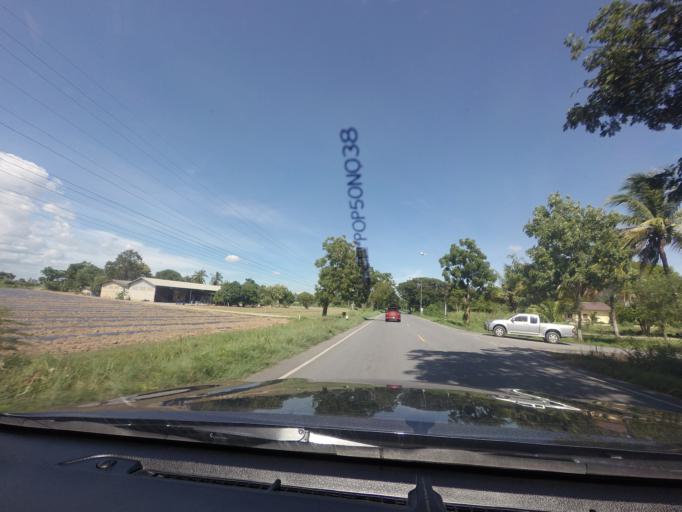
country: TH
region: Kanchanaburi
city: Phanom Thuan
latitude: 14.1728
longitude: 99.8473
